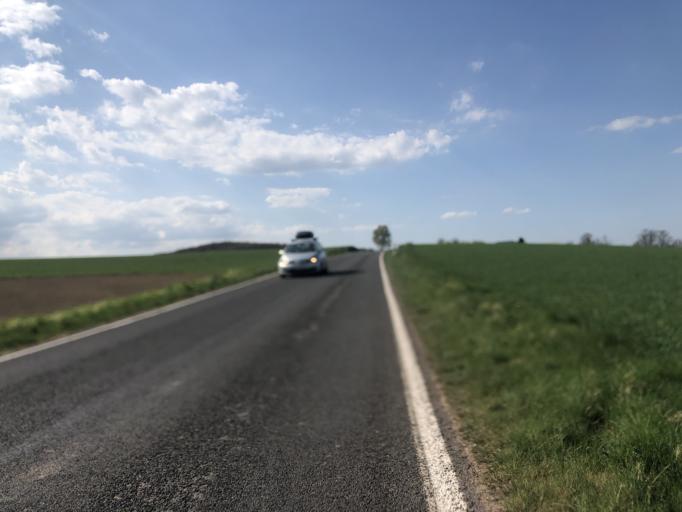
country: DE
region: North Rhine-Westphalia
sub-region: Regierungsbezirk Koln
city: Kall
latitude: 50.6103
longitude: 6.5725
